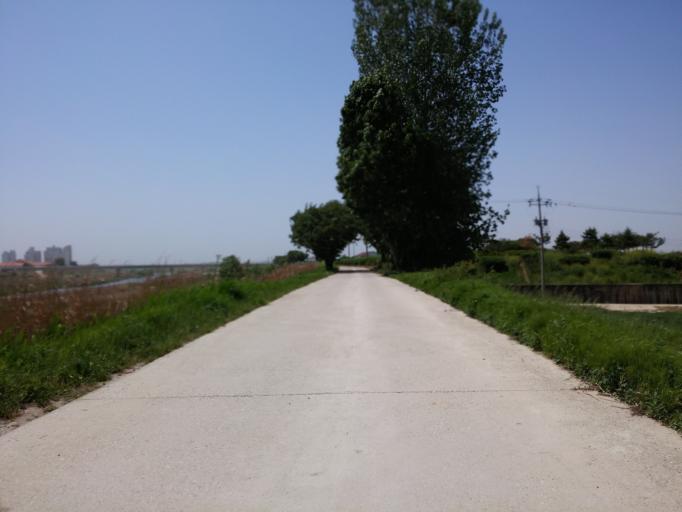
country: KR
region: Chungcheongnam-do
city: Nonsan
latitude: 36.2159
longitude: 127.1053
